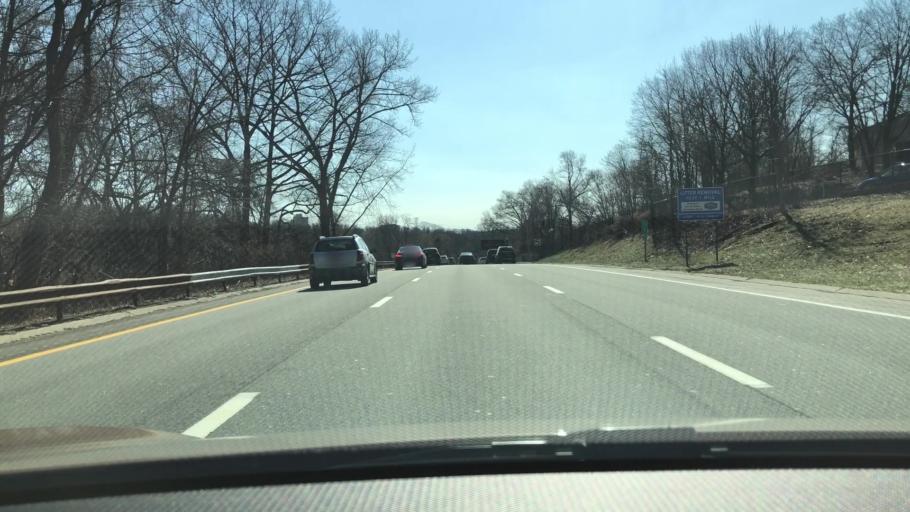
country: US
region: New York
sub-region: Westchester County
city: Tuckahoe
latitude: 40.9617
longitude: -73.8527
